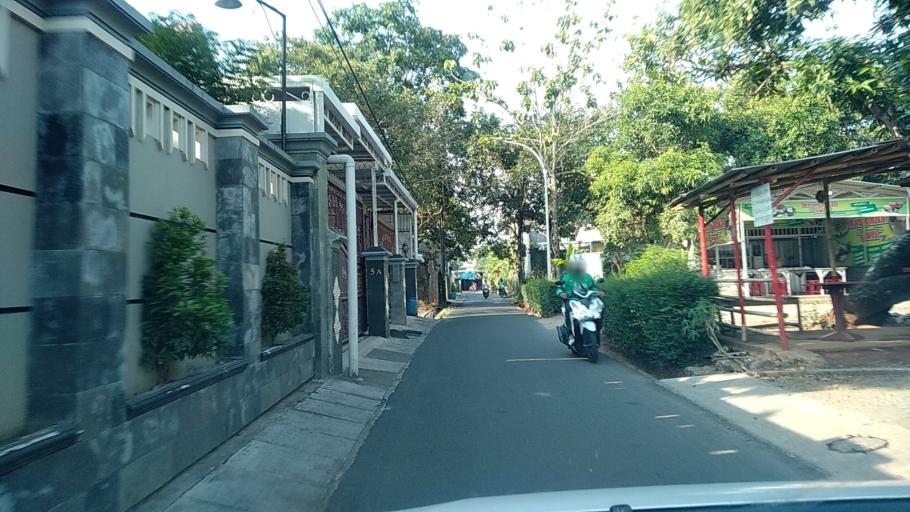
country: ID
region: Central Java
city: Ungaran
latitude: -7.0697
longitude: 110.4345
